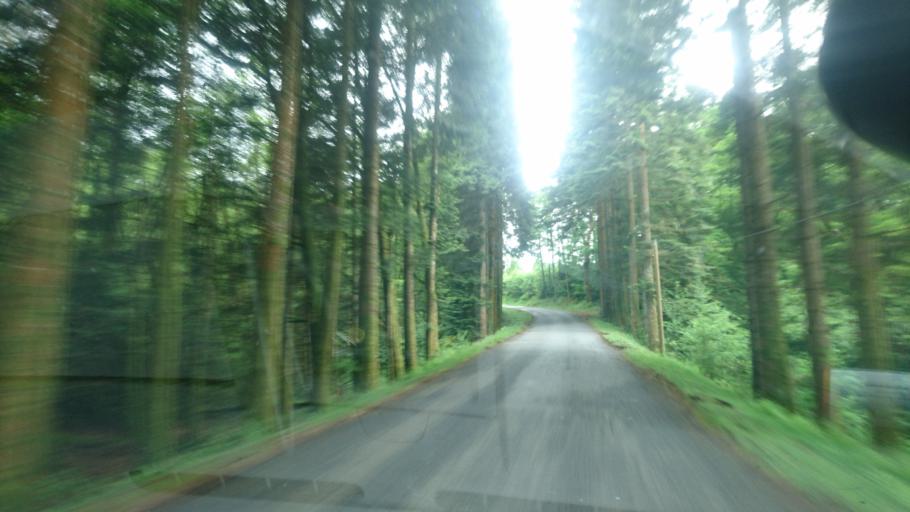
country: FR
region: Limousin
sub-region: Departement de la Haute-Vienne
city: Peyrat-le-Chateau
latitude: 45.8215
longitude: 1.8300
